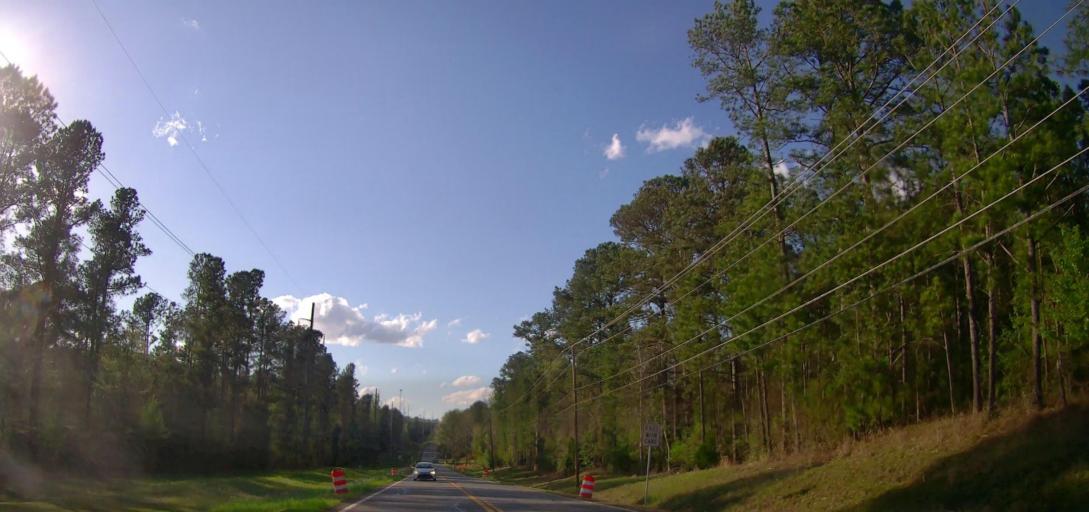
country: US
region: Georgia
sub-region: Baldwin County
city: Milledgeville
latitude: 33.0995
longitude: -83.2706
